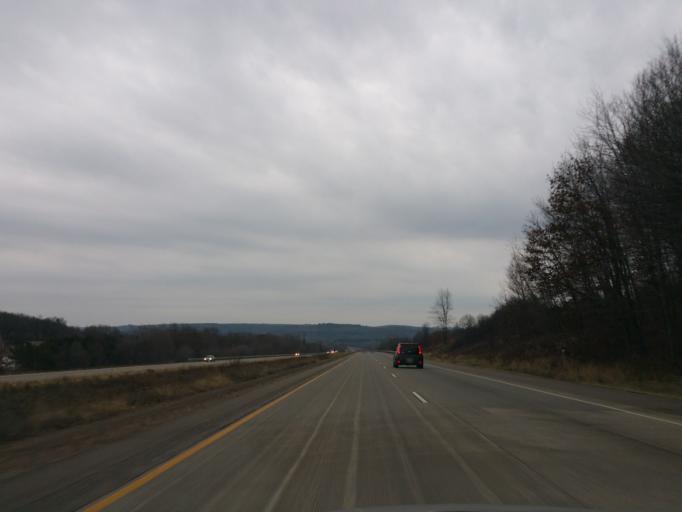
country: US
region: Wisconsin
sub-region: Eau Claire County
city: Eau Claire
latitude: 44.7994
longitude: -91.5538
